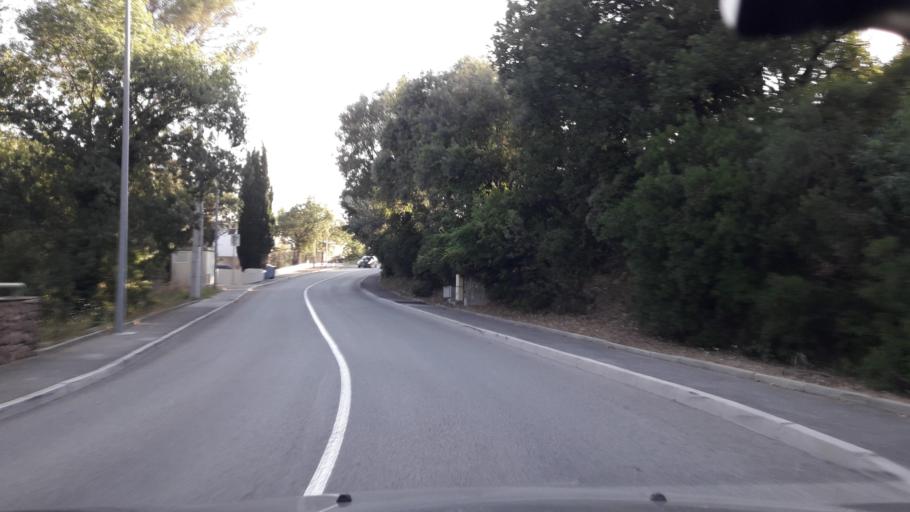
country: FR
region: Provence-Alpes-Cote d'Azur
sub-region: Departement du Var
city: Saint-Raphael
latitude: 43.4431
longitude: 6.7971
